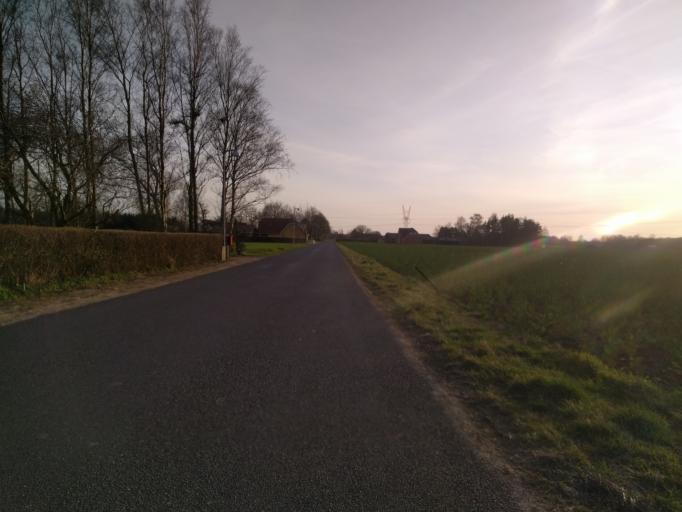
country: DK
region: South Denmark
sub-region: Odense Kommune
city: Bullerup
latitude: 55.4302
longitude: 10.5058
